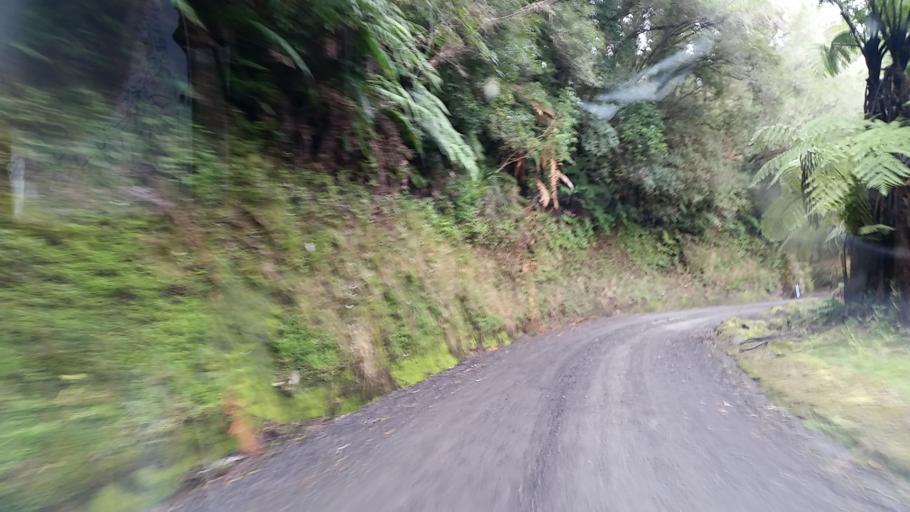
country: NZ
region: Taranaki
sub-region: New Plymouth District
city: Waitara
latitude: -39.1603
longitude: 174.5513
